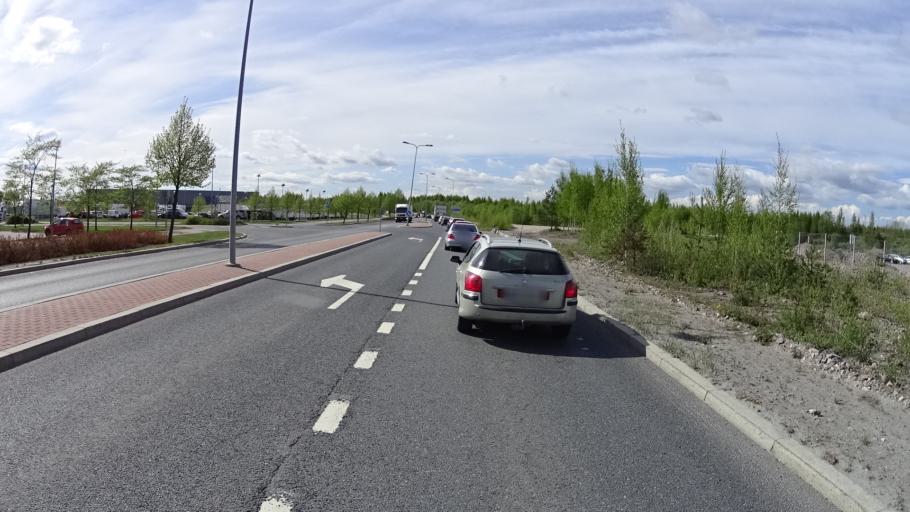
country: FI
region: Uusimaa
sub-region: Helsinki
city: Vantaa
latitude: 60.3025
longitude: 24.9234
